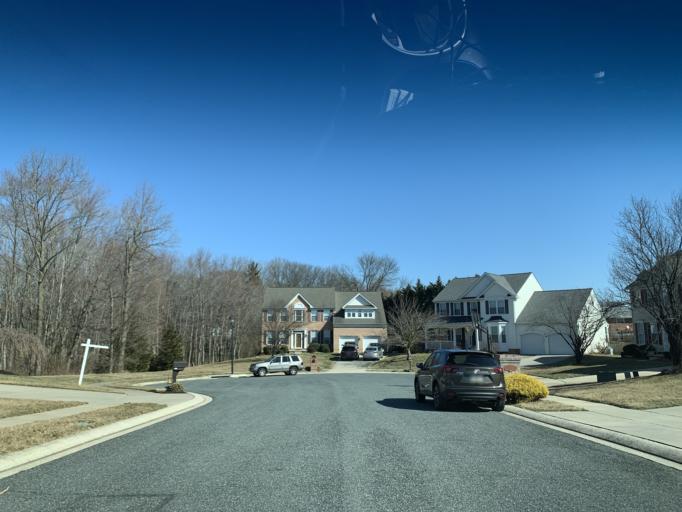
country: US
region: Maryland
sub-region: Harford County
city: South Bel Air
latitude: 39.5400
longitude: -76.3137
